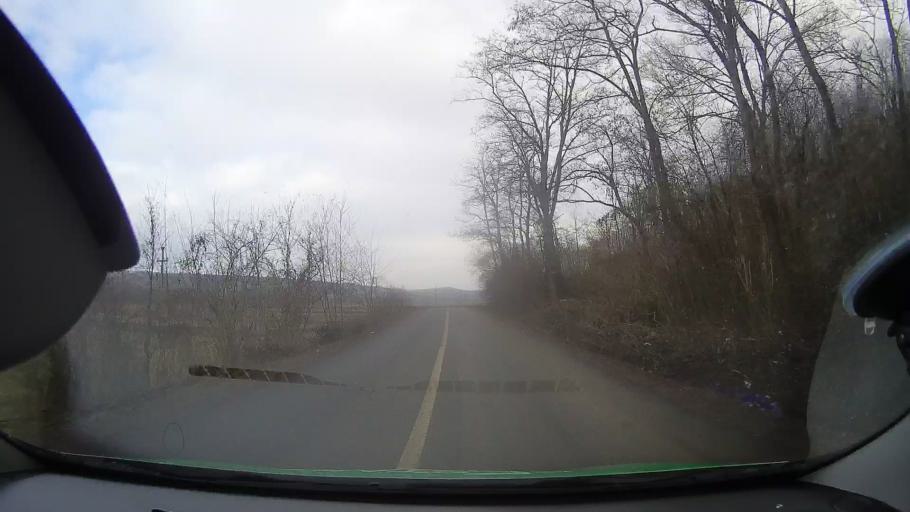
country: RO
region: Mures
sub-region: Comuna Ludus
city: Gheja
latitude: 46.4064
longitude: 24.0659
